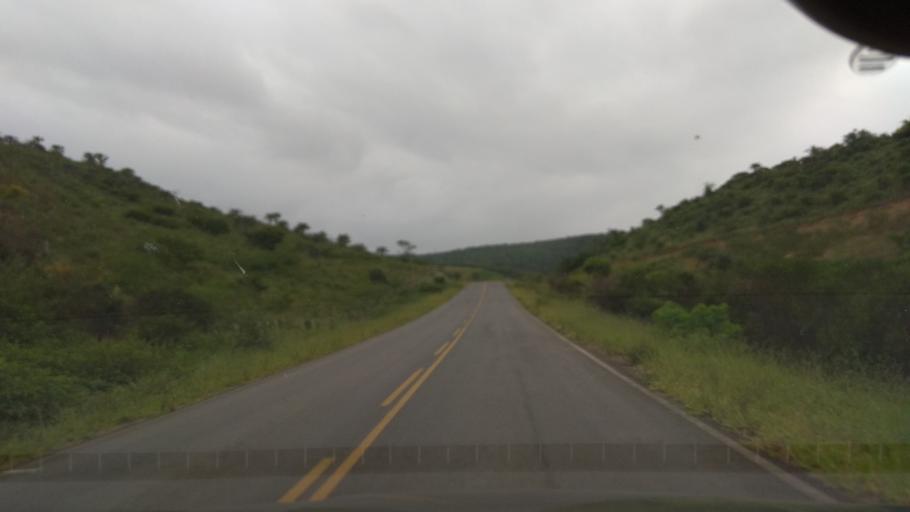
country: BR
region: Bahia
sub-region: Santa Ines
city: Santa Ines
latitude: -13.2682
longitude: -39.7973
